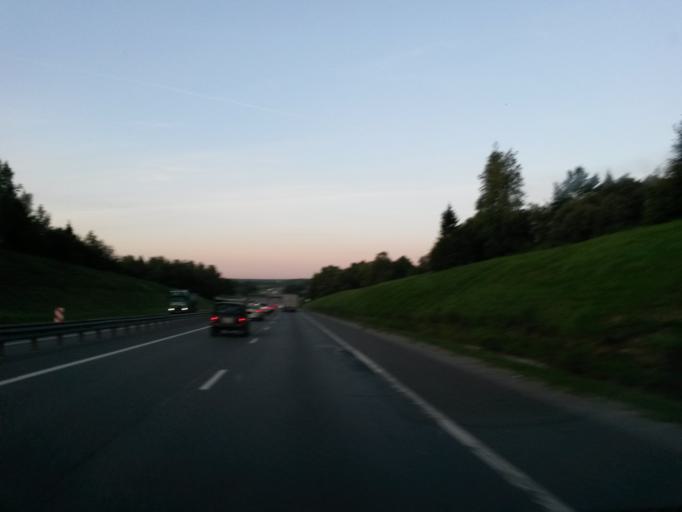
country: RU
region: Moskovskaya
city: Sergiyev Posad
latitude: 56.2835
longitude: 38.2071
